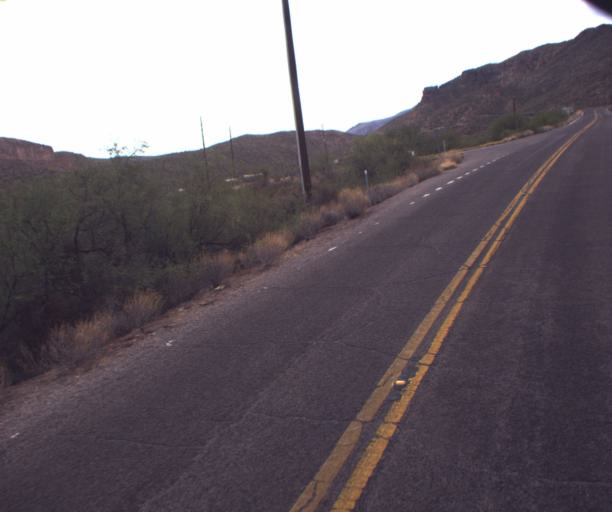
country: US
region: Arizona
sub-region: Pinal County
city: Apache Junction
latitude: 33.5337
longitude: -111.4184
